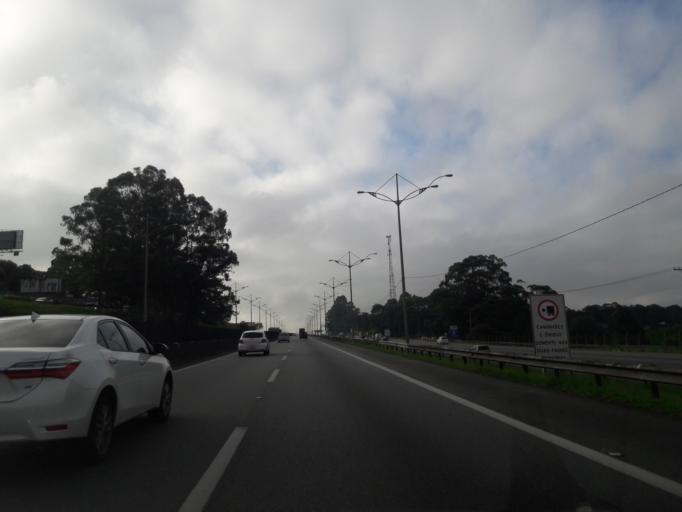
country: BR
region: Sao Paulo
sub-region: Sao Bernardo Do Campo
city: Sao Bernardo do Campo
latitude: -23.6737
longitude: -46.5704
